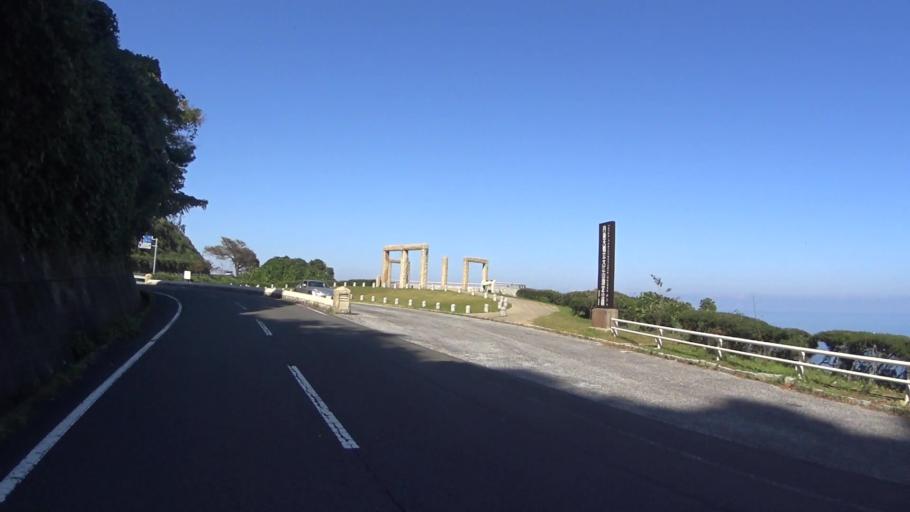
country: JP
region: Kyoto
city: Miyazu
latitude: 35.7569
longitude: 135.2457
